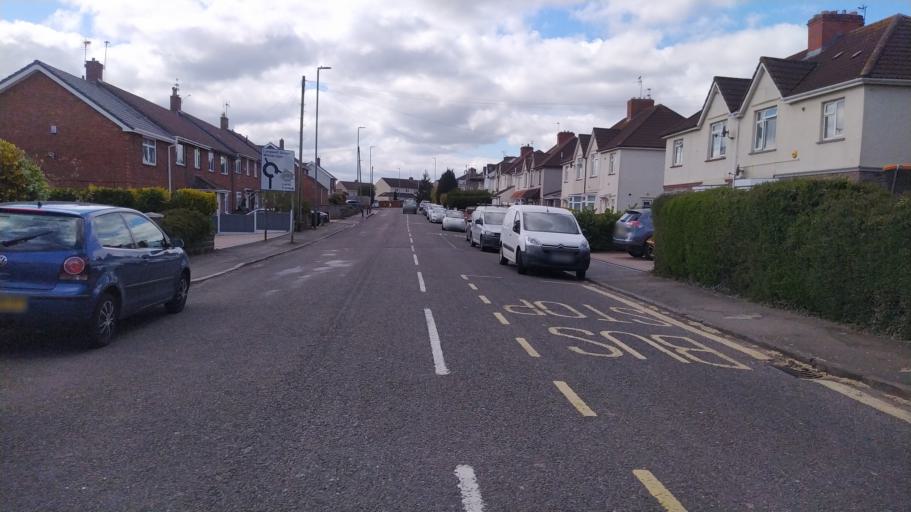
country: GB
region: England
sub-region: South Gloucestershire
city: Kingswood
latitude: 51.4437
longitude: -2.4898
